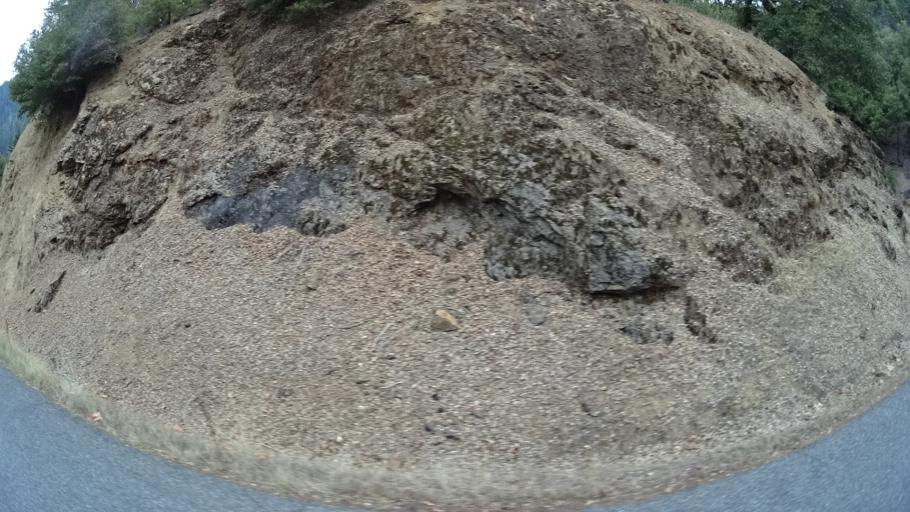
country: US
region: California
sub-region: Siskiyou County
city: Happy Camp
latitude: 41.7581
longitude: -123.3599
